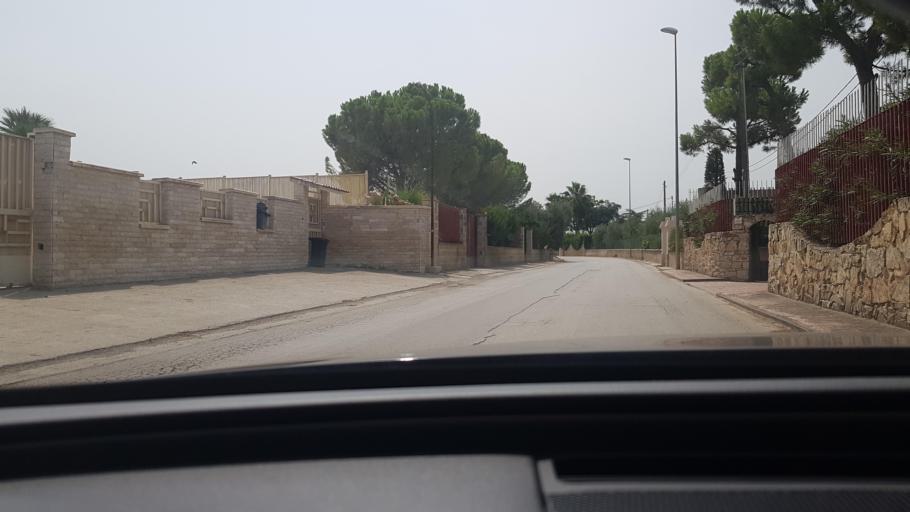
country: IT
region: Apulia
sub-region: Provincia di Barletta - Andria - Trani
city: Andria
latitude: 41.2306
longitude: 16.2683
